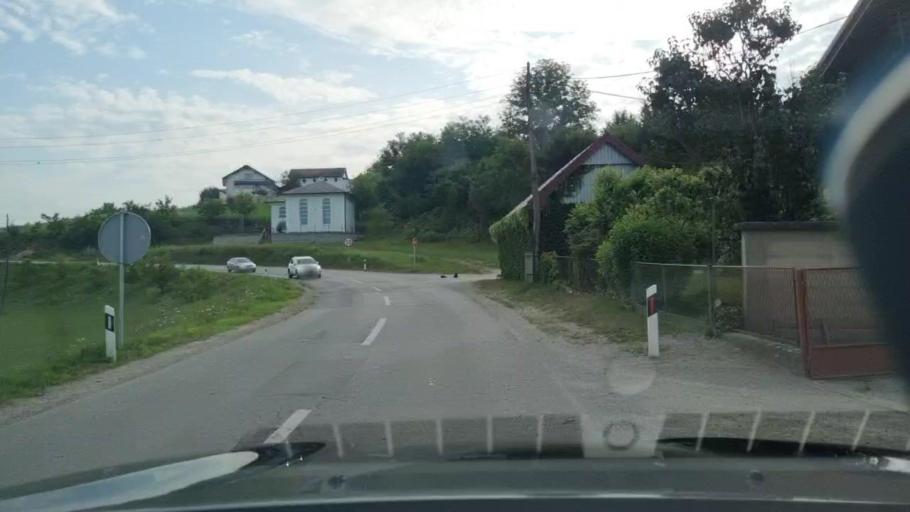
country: BA
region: Federation of Bosnia and Herzegovina
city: Vrnograc
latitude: 45.1611
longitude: 15.9247
